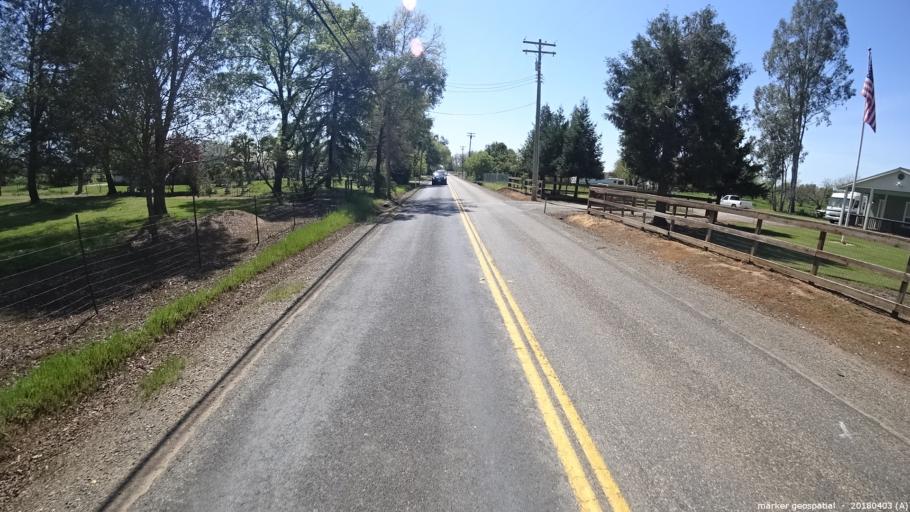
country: US
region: California
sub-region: Sacramento County
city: Wilton
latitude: 38.4014
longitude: -121.2735
